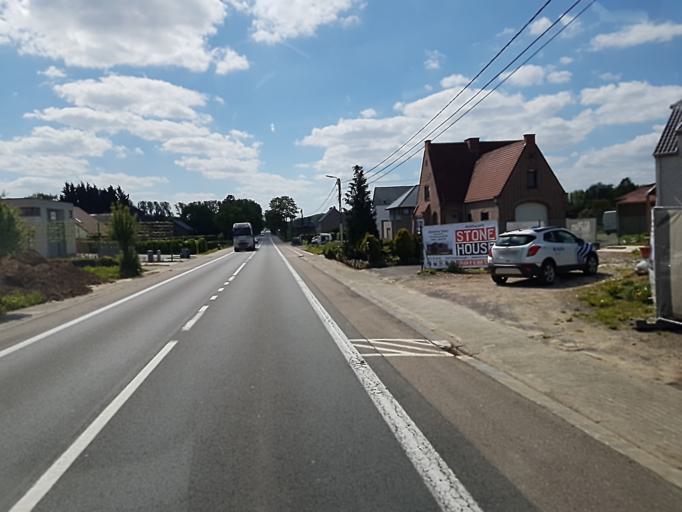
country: BE
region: Flanders
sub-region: Provincie Vlaams-Brabant
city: Glabbeek-Zuurbemde
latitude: 50.8623
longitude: 4.9559
